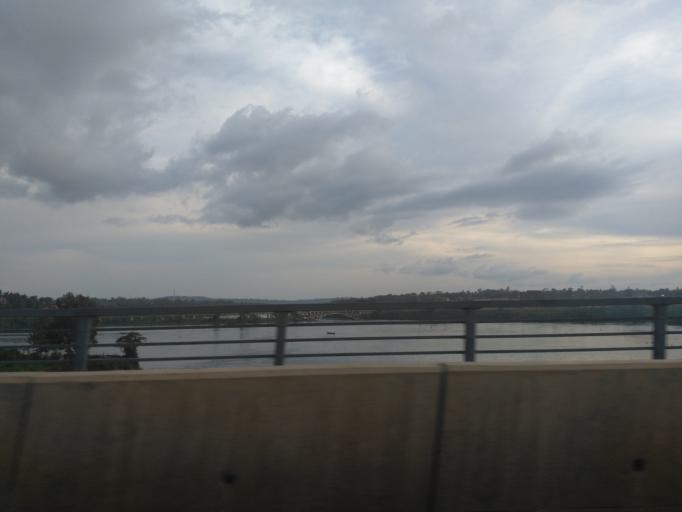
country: UG
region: Eastern Region
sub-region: Jinja District
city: Jinja
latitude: 0.4392
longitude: 33.1902
